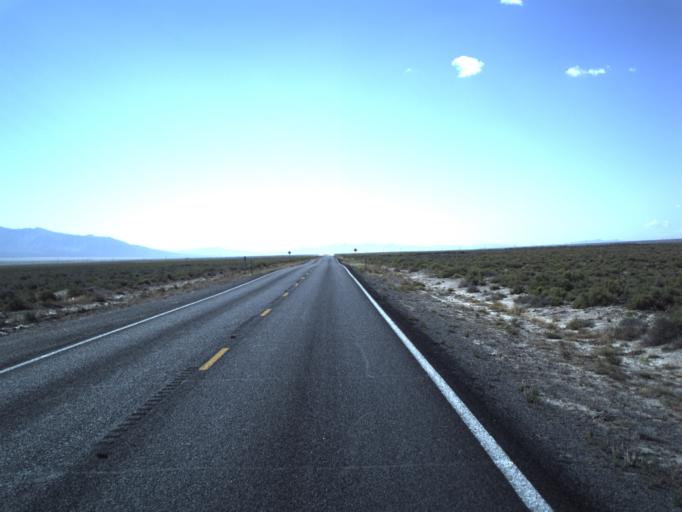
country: US
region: Utah
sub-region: Beaver County
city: Milford
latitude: 38.5400
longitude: -112.9912
